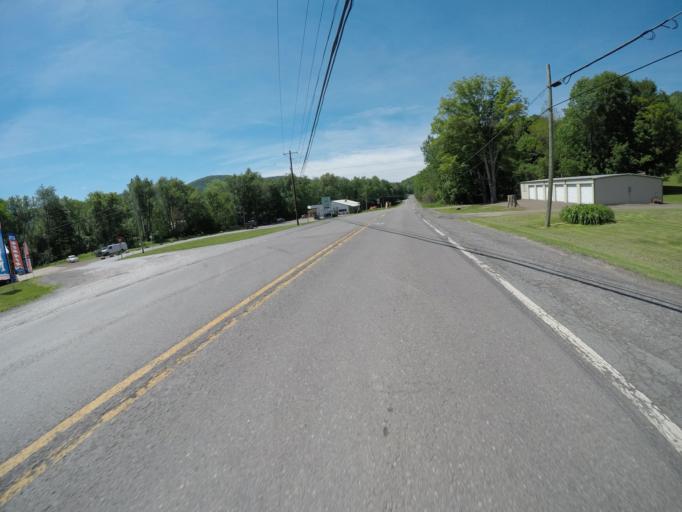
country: US
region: New York
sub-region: Delaware County
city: Delhi
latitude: 42.2089
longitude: -74.9807
